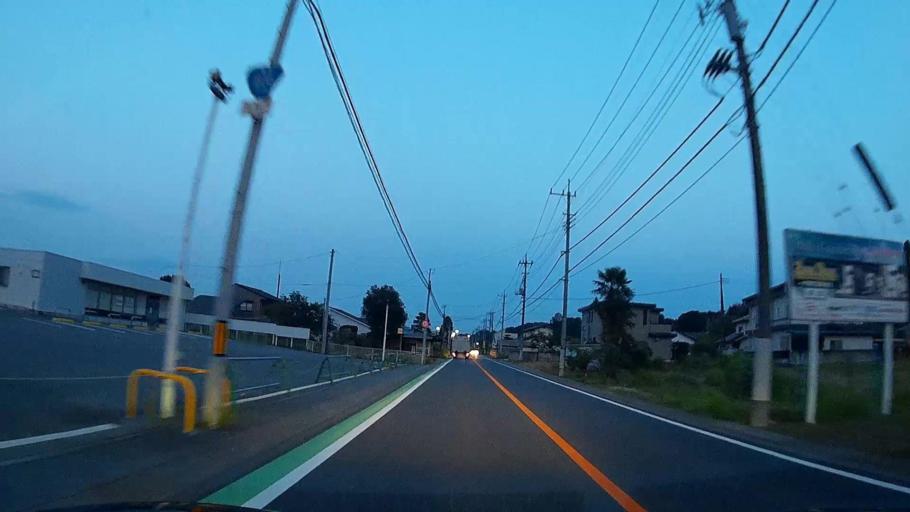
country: JP
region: Gunma
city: Annaka
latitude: 36.3552
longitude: 138.9287
